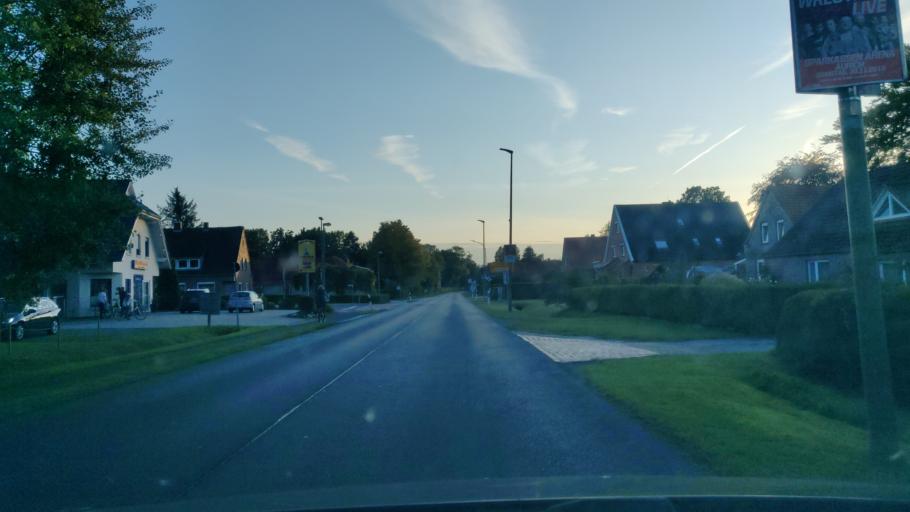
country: DE
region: Lower Saxony
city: Aurich
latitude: 53.4445
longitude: 7.4198
